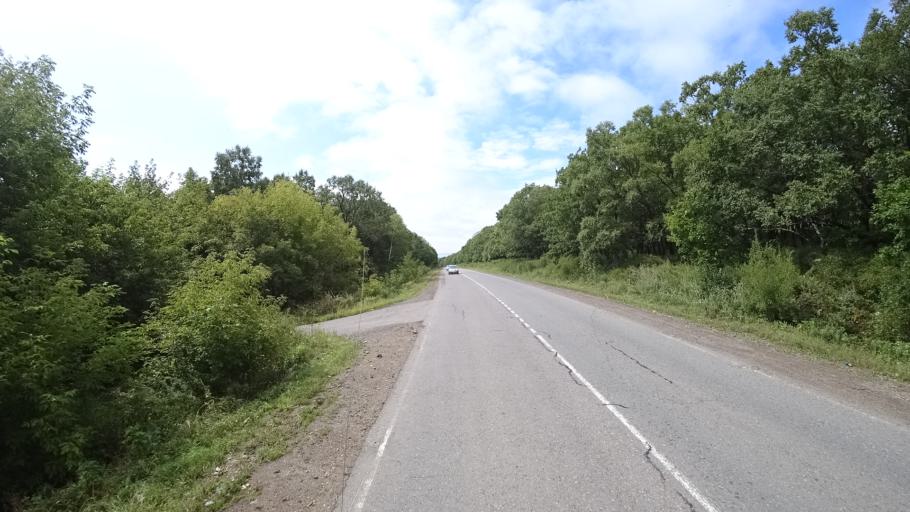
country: RU
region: Primorskiy
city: Lyalichi
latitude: 44.1396
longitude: 132.4209
